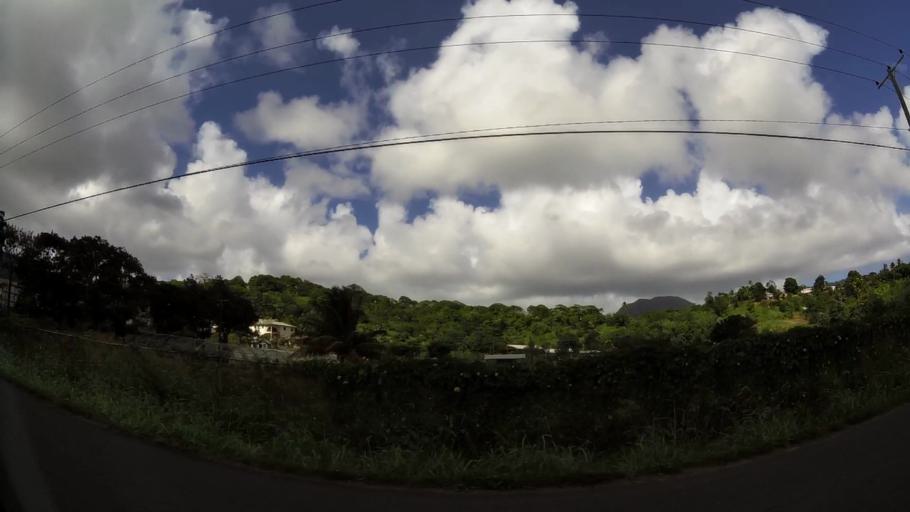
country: LC
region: Dennery Quarter
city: Dennery
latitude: 13.9330
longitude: -60.9278
